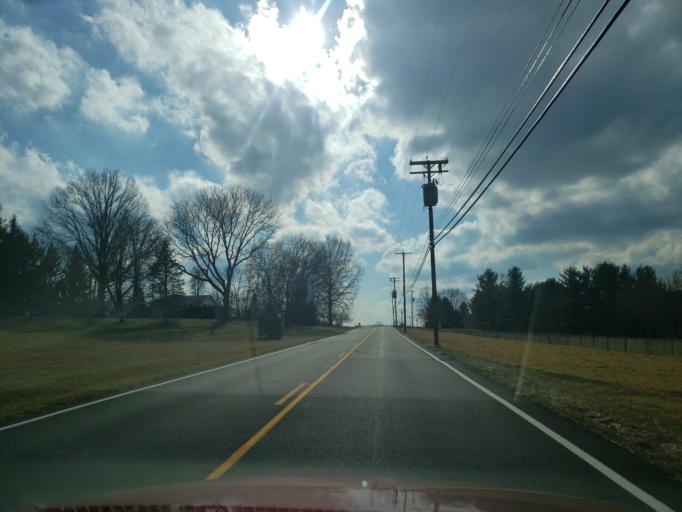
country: US
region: New Jersey
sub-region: Hunterdon County
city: Lambertville
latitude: 40.4335
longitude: -74.9544
